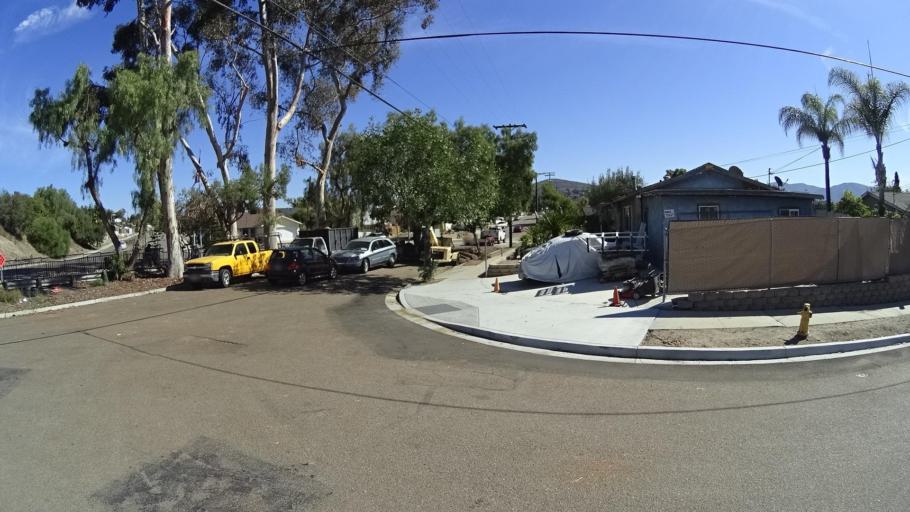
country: US
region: California
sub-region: San Diego County
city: Lemon Grove
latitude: 32.7248
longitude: -117.0211
